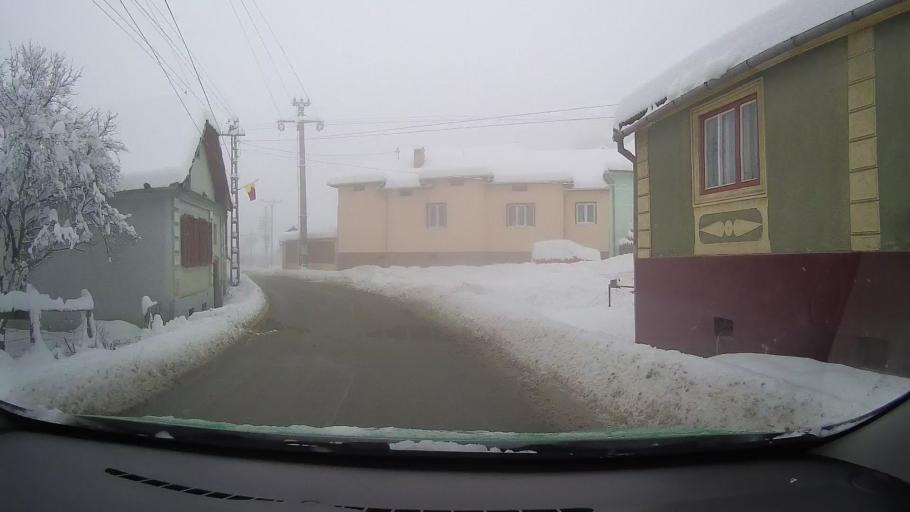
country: RO
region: Sibiu
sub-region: Comuna Poiana Sibiului
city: Poiana Sibiului
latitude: 45.8016
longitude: 23.7781
